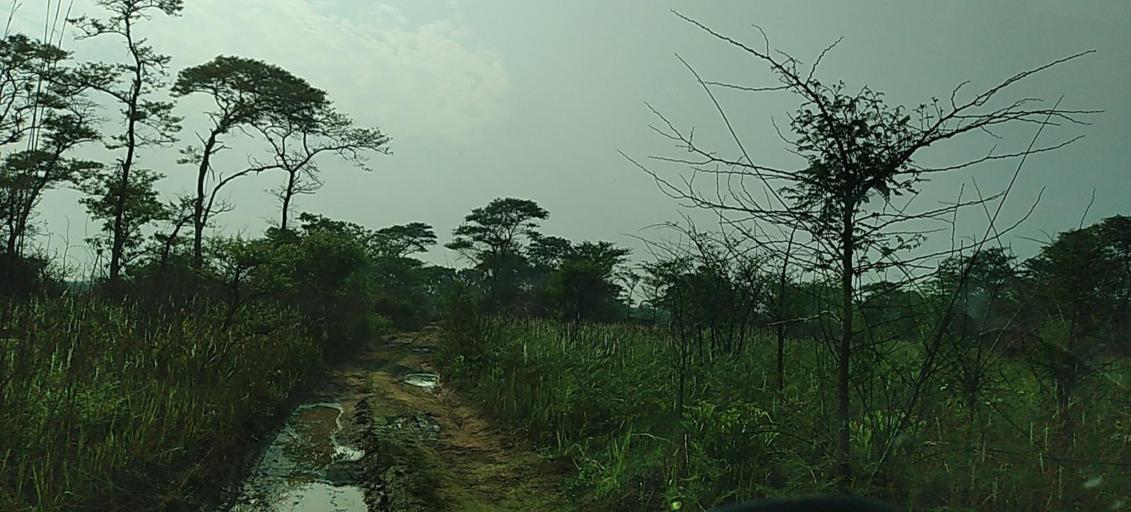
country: ZM
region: North-Western
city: Solwezi
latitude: -12.3945
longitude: 26.5793
